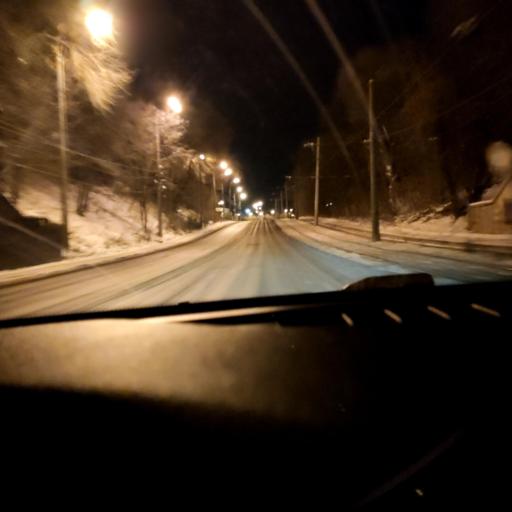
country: RU
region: Samara
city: Smyshlyayevka
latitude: 53.2227
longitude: 50.2832
